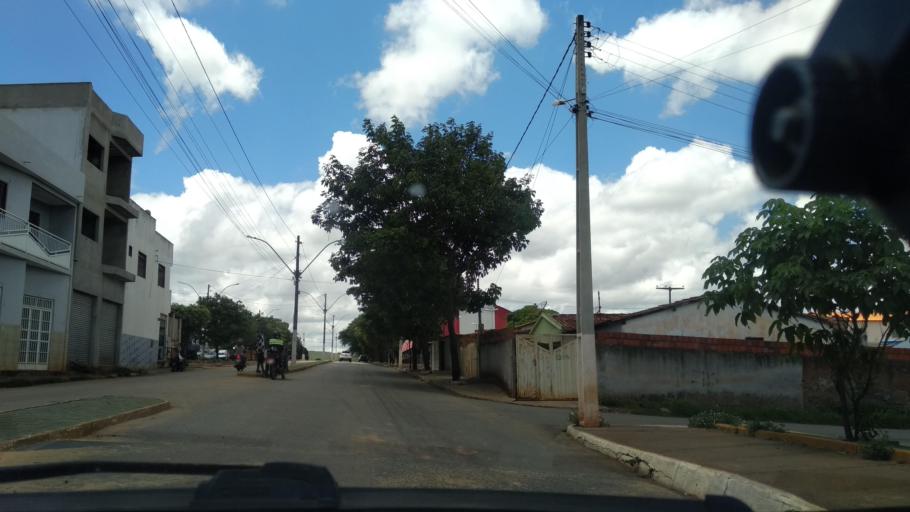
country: BR
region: Bahia
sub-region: Caetite
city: Caetite
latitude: -14.0556
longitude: -42.4841
